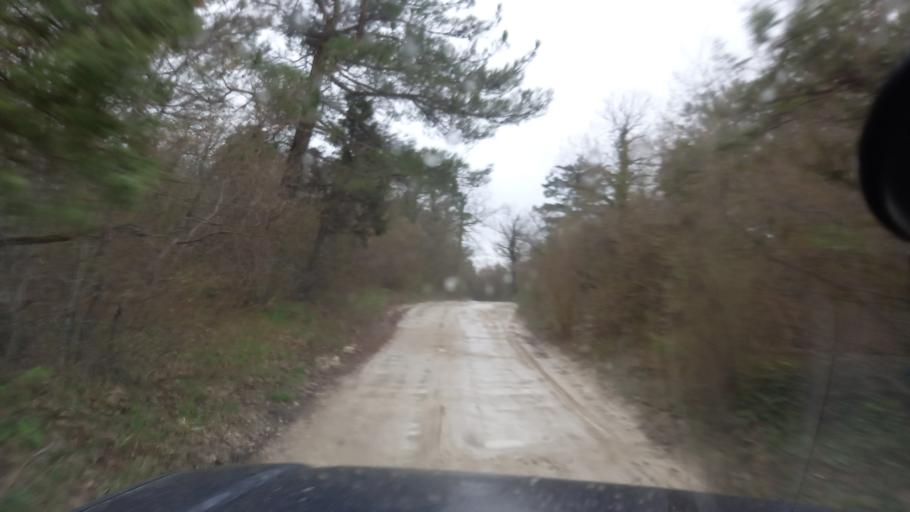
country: RU
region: Krasnodarskiy
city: Dzhubga
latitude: 44.3220
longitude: 38.6882
